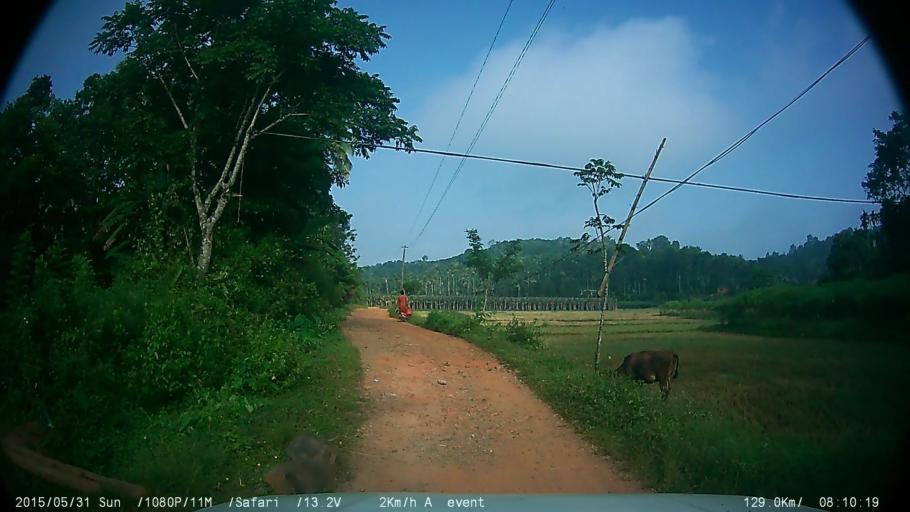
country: IN
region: Kerala
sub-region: Wayanad
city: Kalpetta
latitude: 11.6393
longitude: 76.0206
